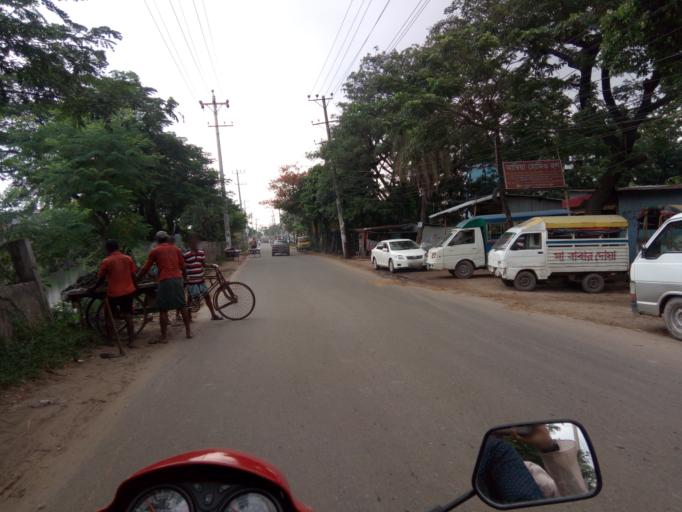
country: BD
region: Dhaka
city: Paltan
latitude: 23.7152
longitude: 90.4587
